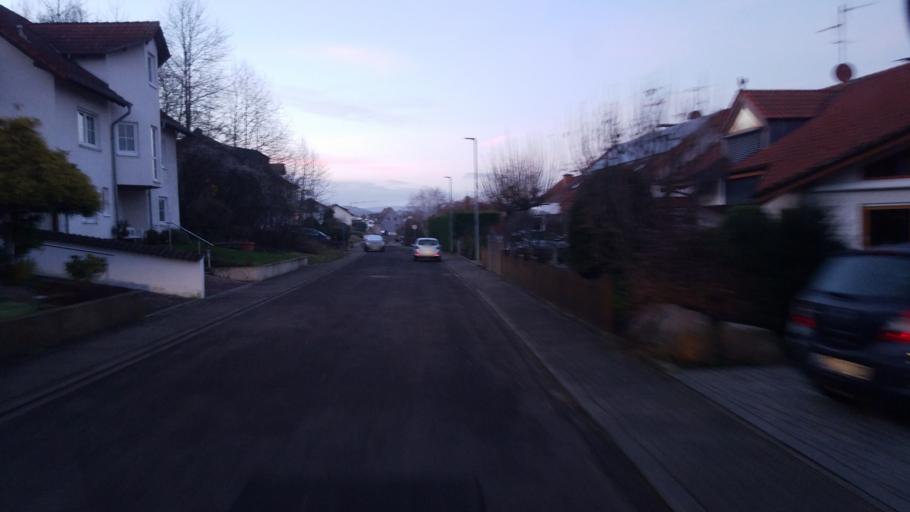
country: DE
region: Rheinland-Pfalz
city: Windesheim
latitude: 49.8917
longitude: 7.8358
